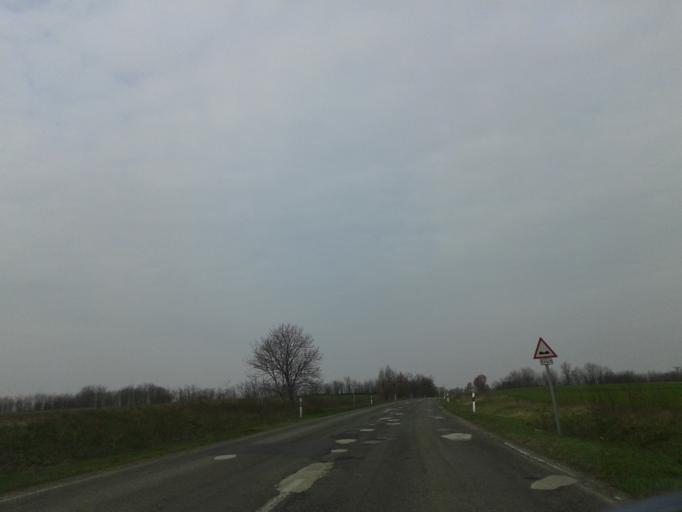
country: HU
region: Komarom-Esztergom
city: Acs
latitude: 47.7220
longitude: 18.0243
